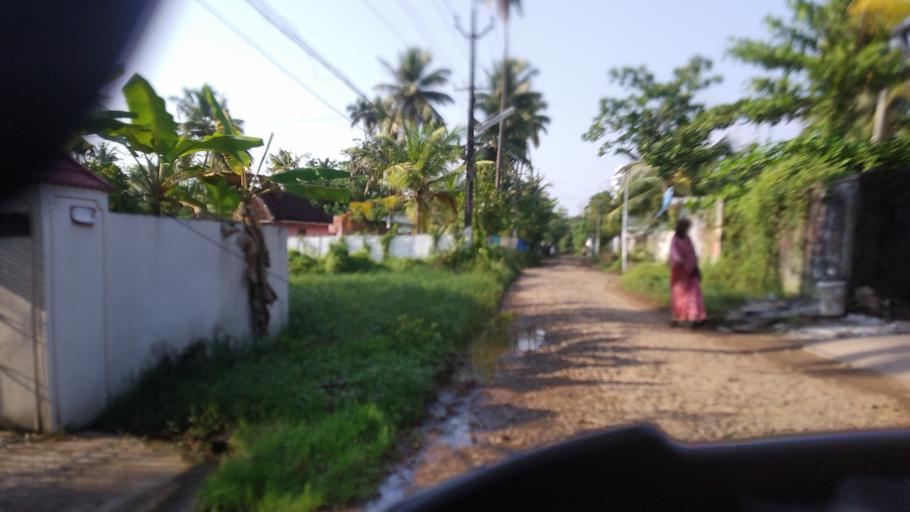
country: IN
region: Kerala
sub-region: Ernakulam
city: Cochin
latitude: 10.0102
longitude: 76.2182
